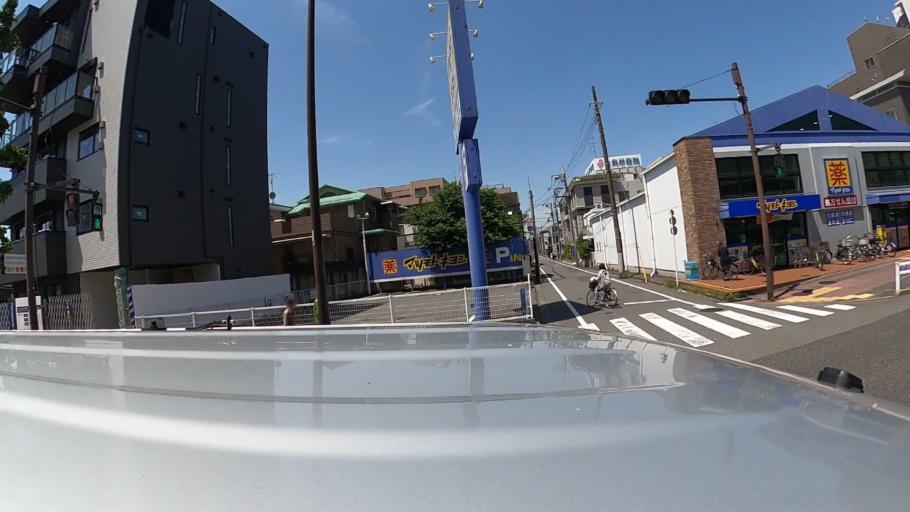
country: JP
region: Kanagawa
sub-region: Kawasaki-shi
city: Kawasaki
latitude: 35.5556
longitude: 139.7395
